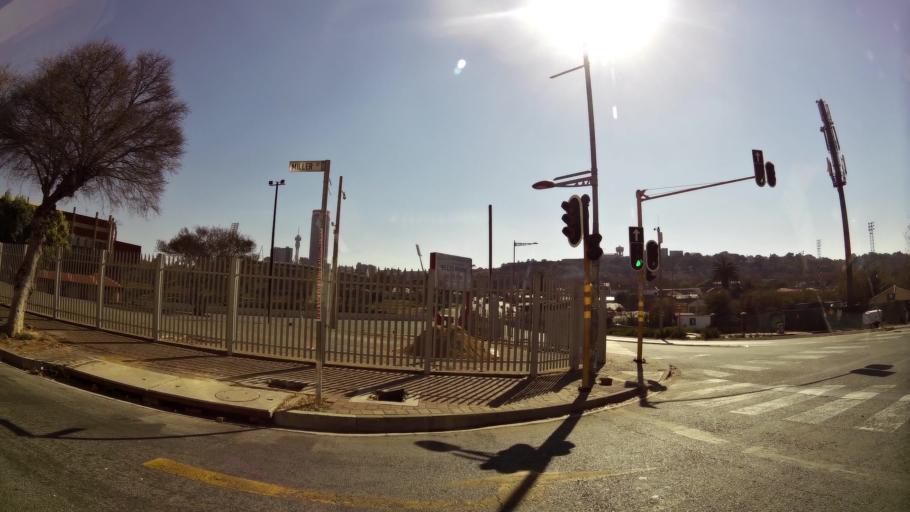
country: ZA
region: Gauteng
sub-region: City of Johannesburg Metropolitan Municipality
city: Johannesburg
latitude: -26.1957
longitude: 28.0661
